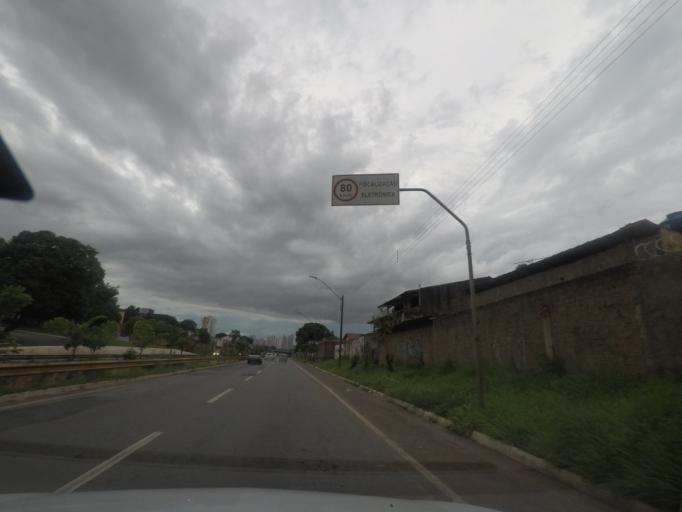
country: BR
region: Goias
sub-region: Goiania
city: Goiania
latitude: -16.6812
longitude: -49.2482
